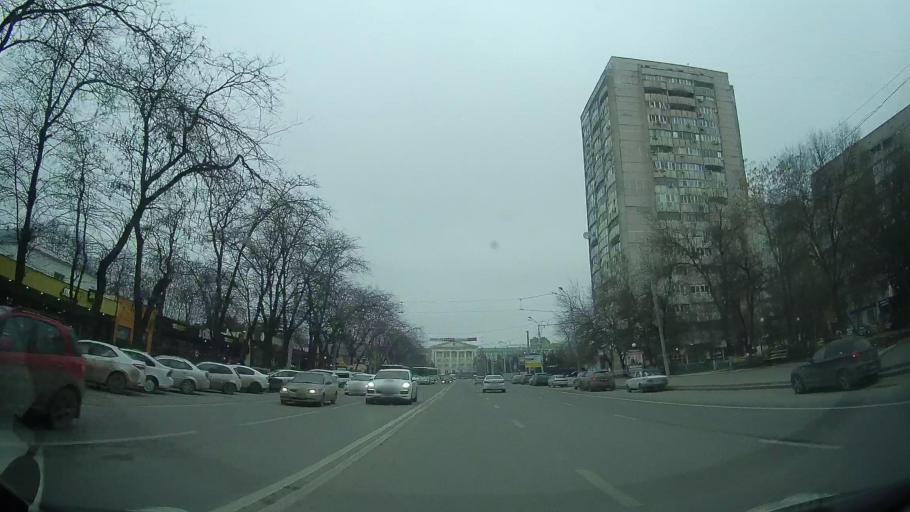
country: RU
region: Rostov
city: Rostov-na-Donu
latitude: 47.2338
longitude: 39.7138
